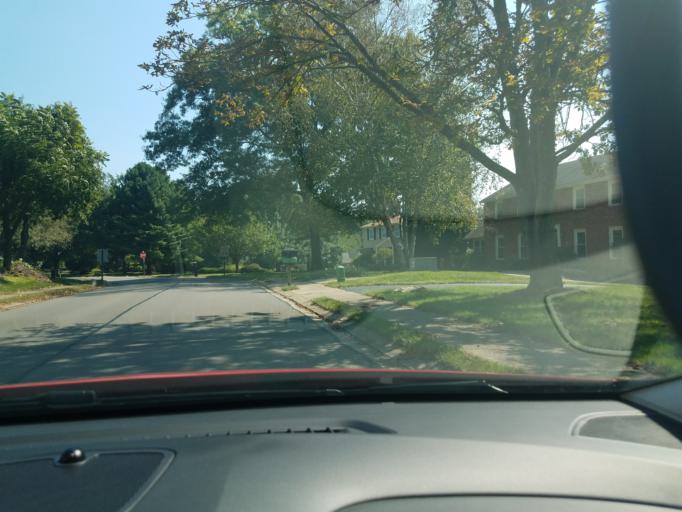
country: US
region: Pennsylvania
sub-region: Allegheny County
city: Franklin Park
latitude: 40.5666
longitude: -80.0750
